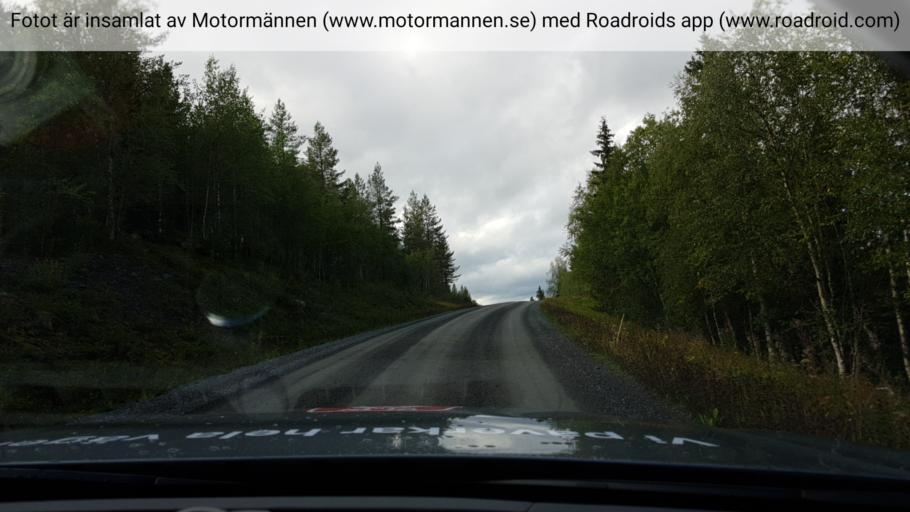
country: SE
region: Jaemtland
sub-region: Krokoms Kommun
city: Krokom
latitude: 63.7355
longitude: 14.4917
